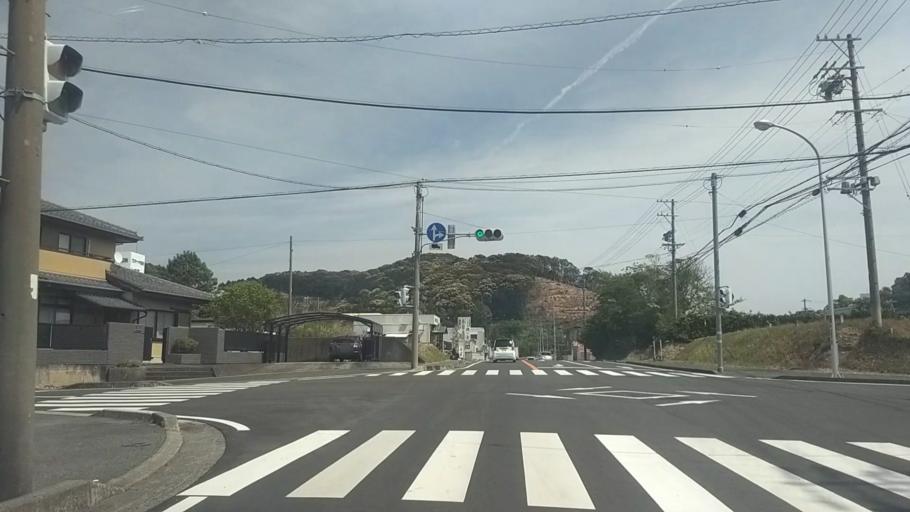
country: JP
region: Shizuoka
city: Kosai-shi
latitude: 34.8005
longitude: 137.5589
